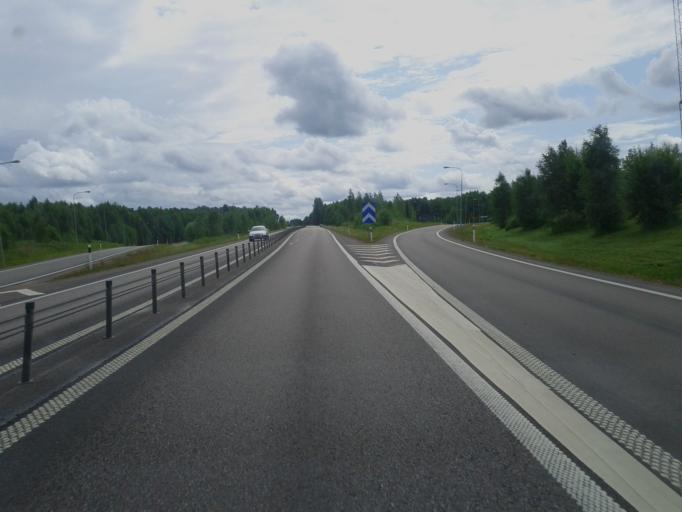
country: SE
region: Dalarna
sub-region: Borlange Kommun
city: Ornas
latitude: 60.4400
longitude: 15.5069
